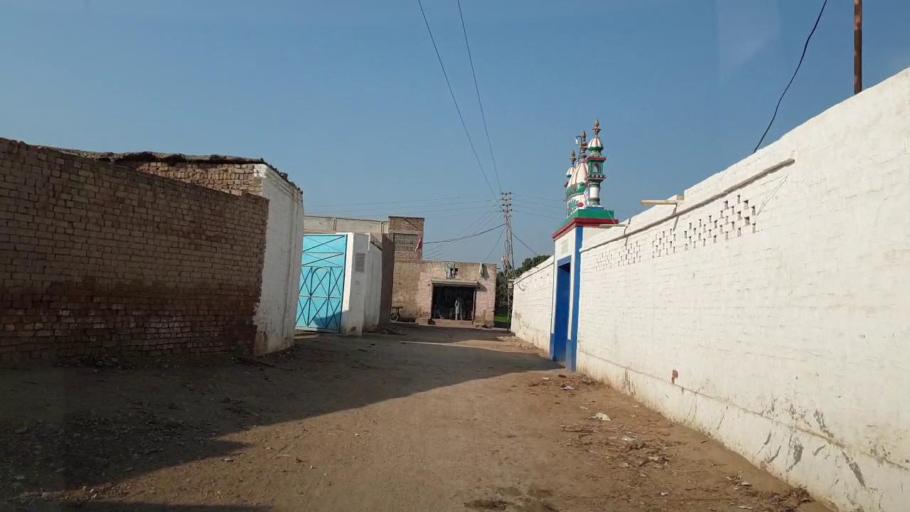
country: PK
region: Sindh
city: Tando Jam
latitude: 25.4730
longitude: 68.5405
